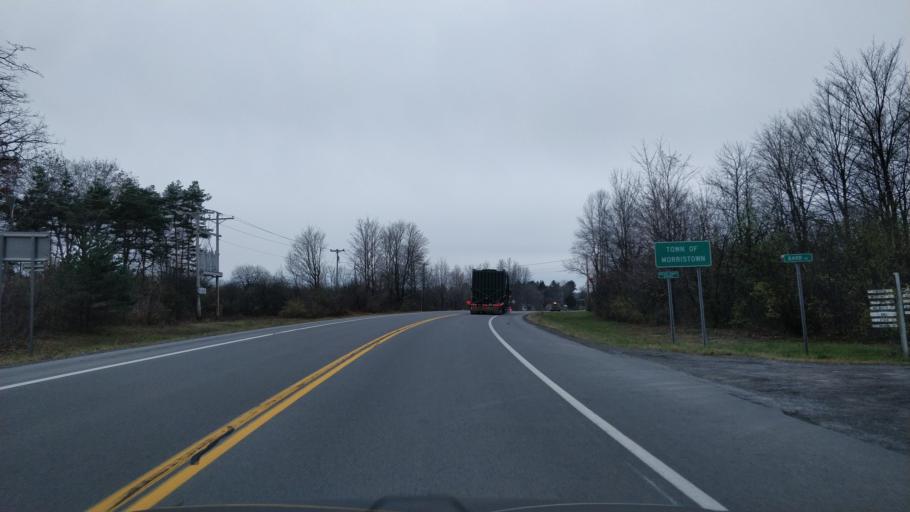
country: CA
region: Ontario
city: Brockville
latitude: 44.6140
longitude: -75.5991
